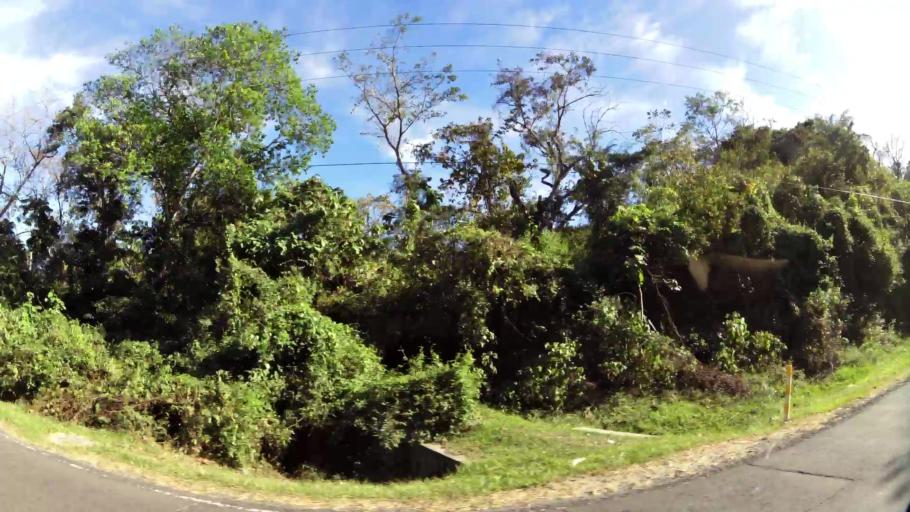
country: SV
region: Cuscatlan
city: Tecoluca
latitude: 13.8201
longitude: -89.0328
